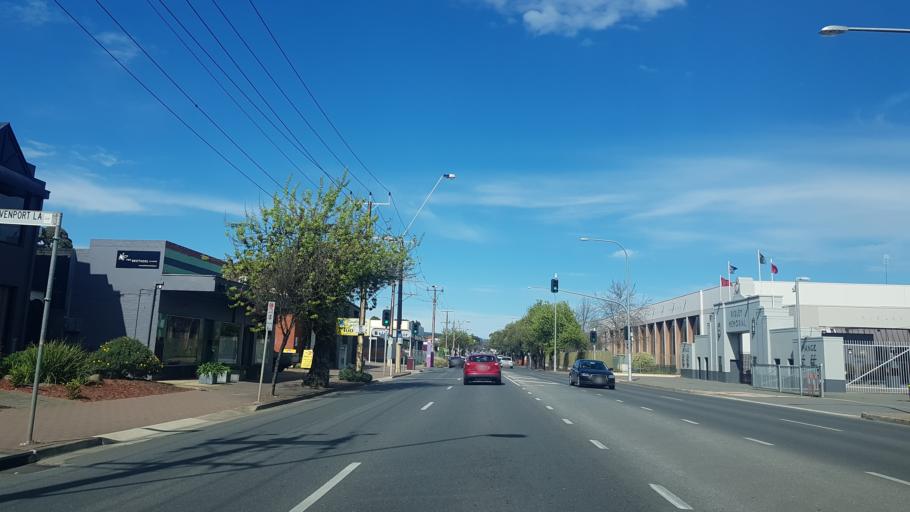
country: AU
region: South Australia
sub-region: Unley
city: Wayville
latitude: -34.9447
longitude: 138.5892
